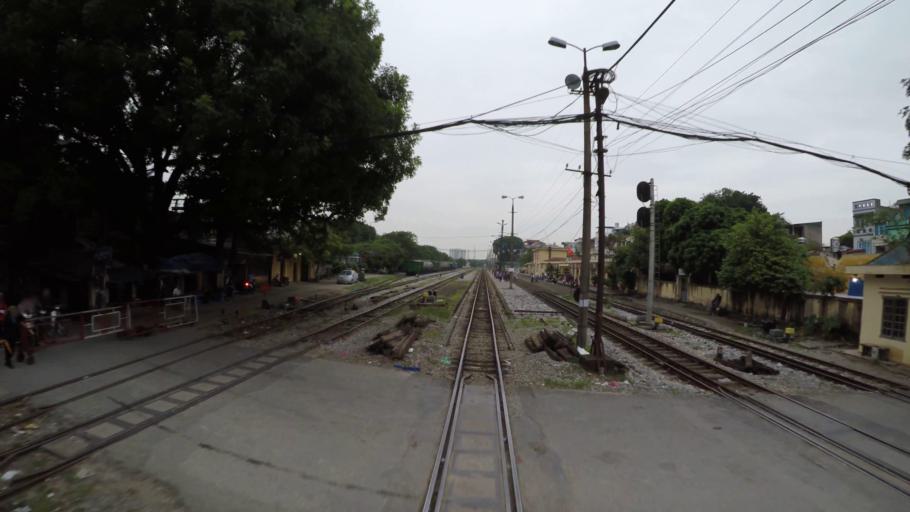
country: VN
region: Ha Noi
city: Trau Quy
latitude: 21.0340
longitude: 105.9051
